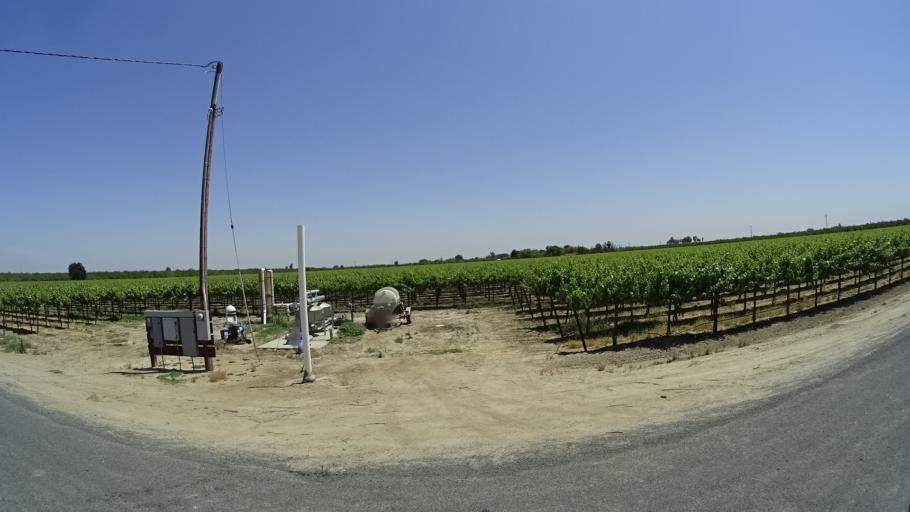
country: US
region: California
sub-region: Kings County
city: Armona
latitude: 36.2709
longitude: -119.7269
